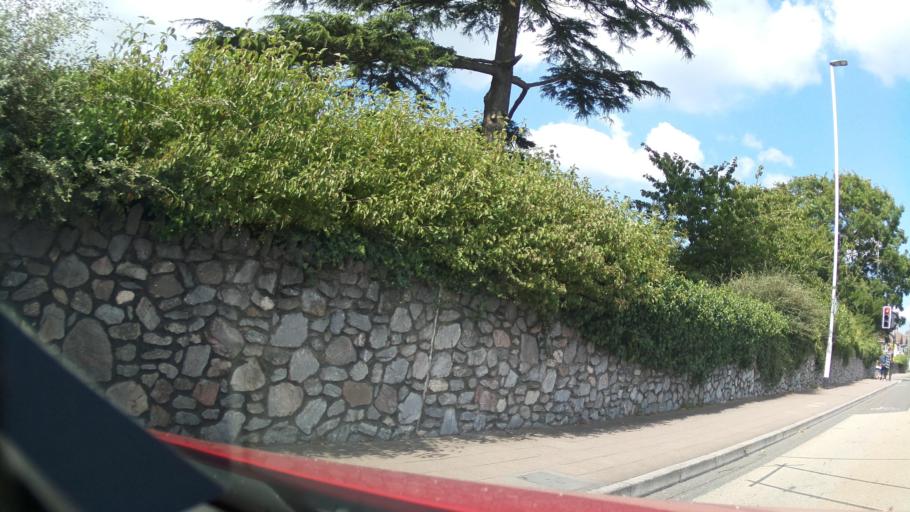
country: GB
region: England
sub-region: Plymouth
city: Plymouth
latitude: 50.3865
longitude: -4.1559
